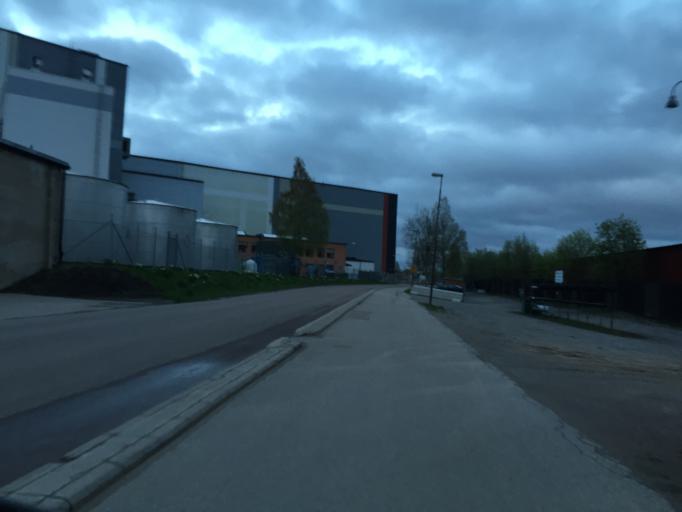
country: SE
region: Dalarna
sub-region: Ludvika Kommun
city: Ludvika
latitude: 60.1415
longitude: 15.1717
